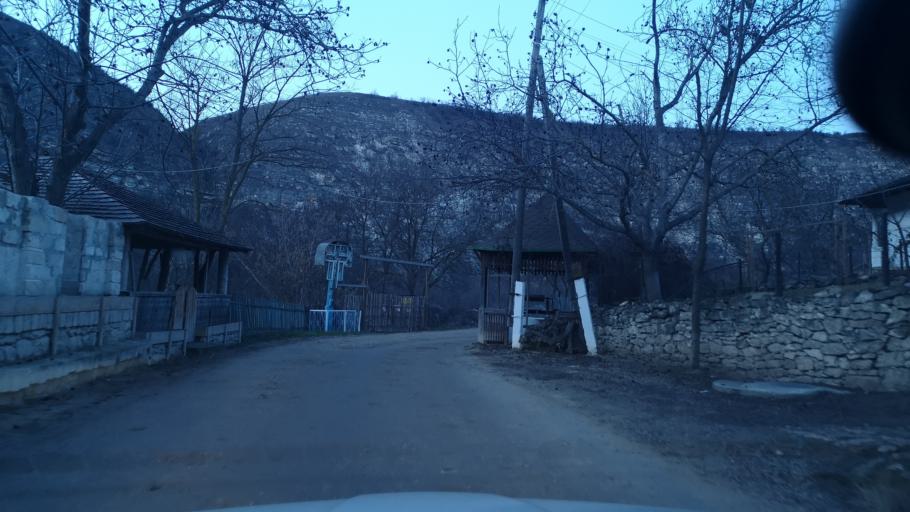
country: MD
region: Telenesti
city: Cocieri
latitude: 47.3058
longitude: 28.9611
